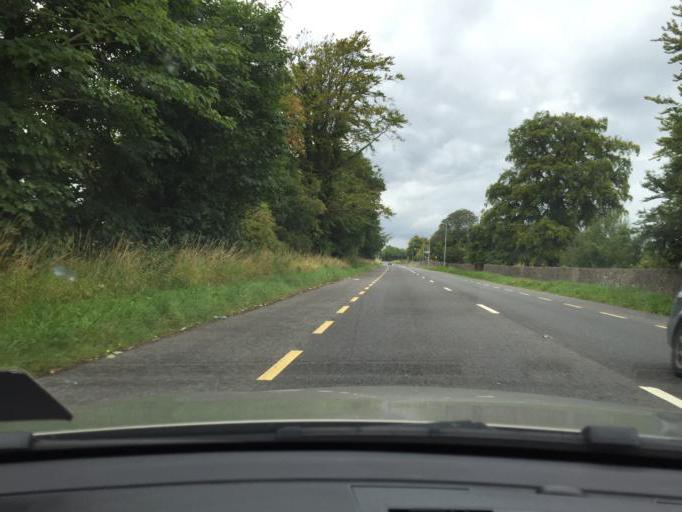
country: IE
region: Leinster
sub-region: Kildare
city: Celbridge
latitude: 53.3776
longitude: -6.5507
